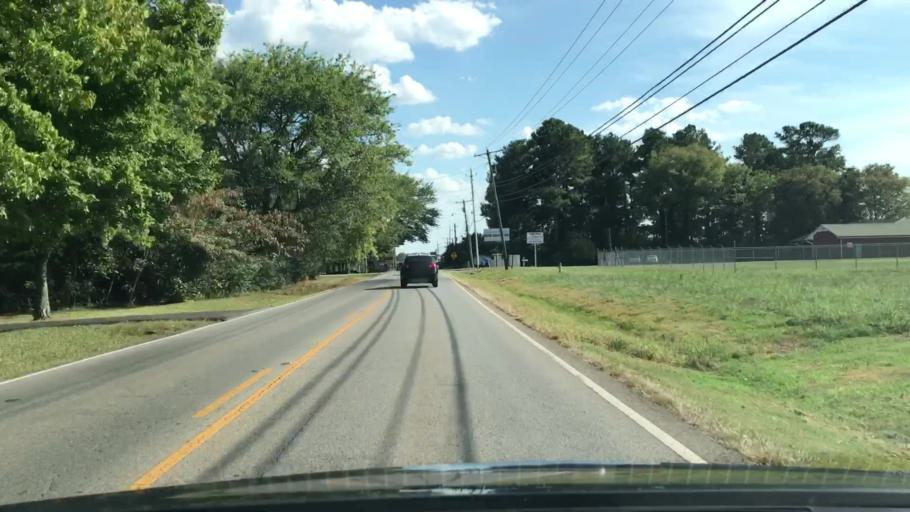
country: US
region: Alabama
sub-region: Madison County
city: Harvest
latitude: 34.8112
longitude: -86.7492
